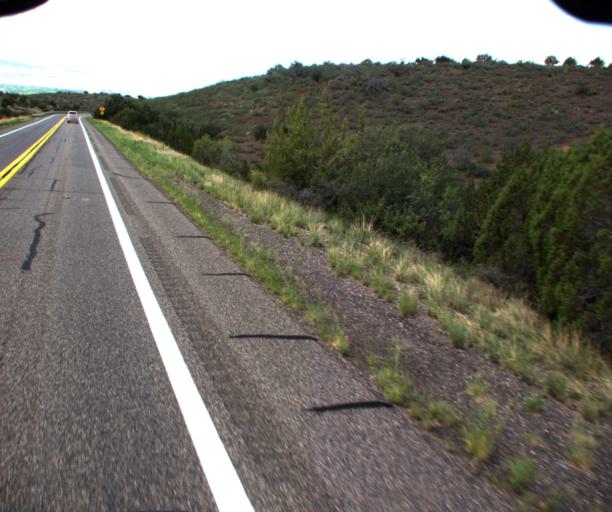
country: US
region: Arizona
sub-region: Yavapai County
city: Lake Montezuma
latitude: 34.4934
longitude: -111.7120
